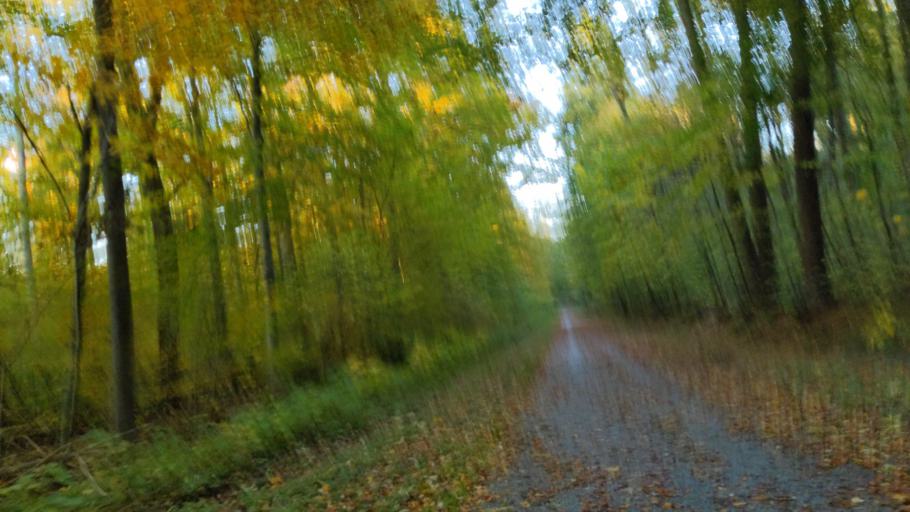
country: DE
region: Schleswig-Holstein
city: Bad Schwartau
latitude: 53.8911
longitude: 10.7511
